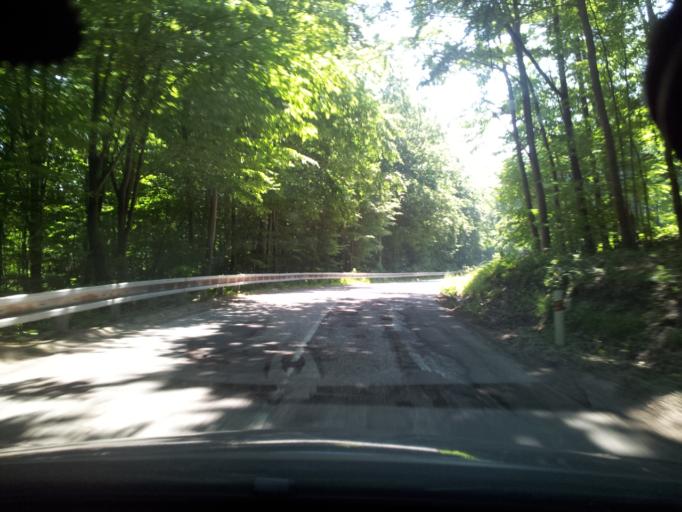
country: SK
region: Nitriansky
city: Partizanske
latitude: 48.5614
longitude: 18.4517
